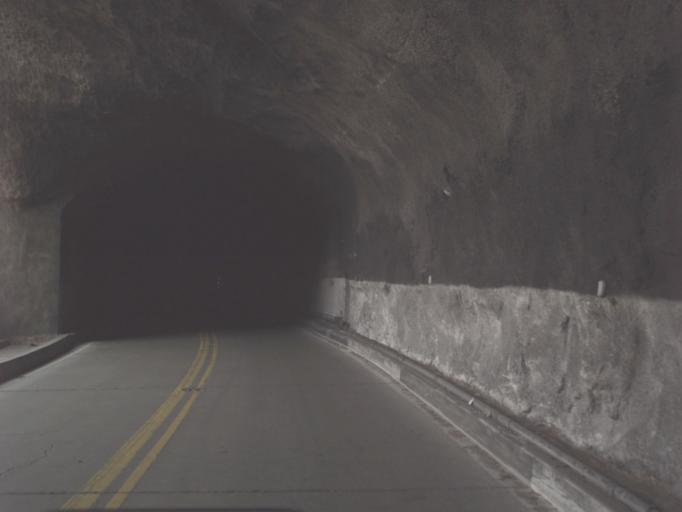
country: US
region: Utah
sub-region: Washington County
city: Hildale
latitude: 37.2099
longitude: -112.9566
